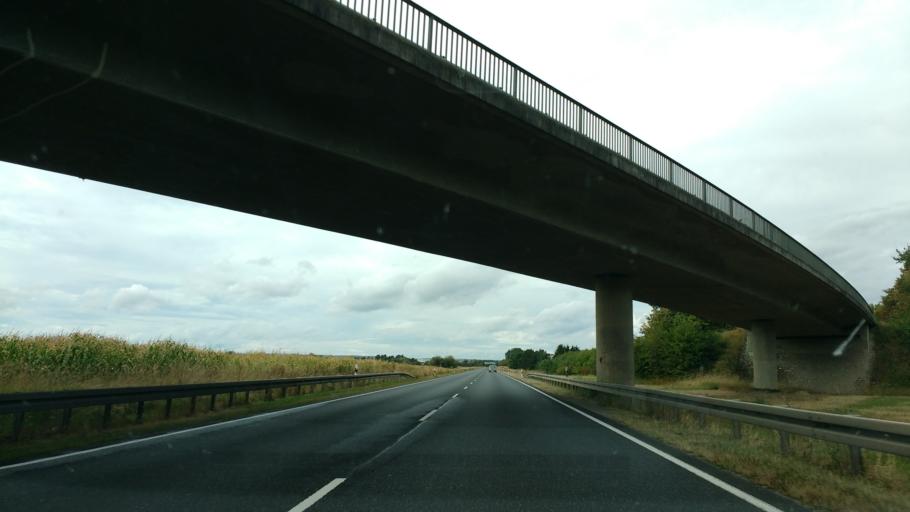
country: DE
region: Bavaria
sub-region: Regierungsbezirk Unterfranken
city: Schwebheim
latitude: 49.9742
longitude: 10.2561
